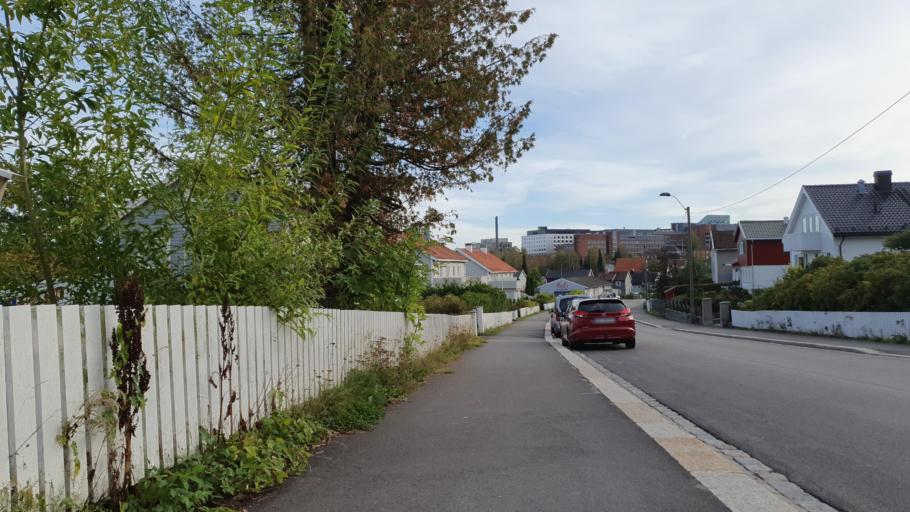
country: NO
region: Vestfold
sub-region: Tonsberg
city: Tonsberg
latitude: 59.2784
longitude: 10.4204
